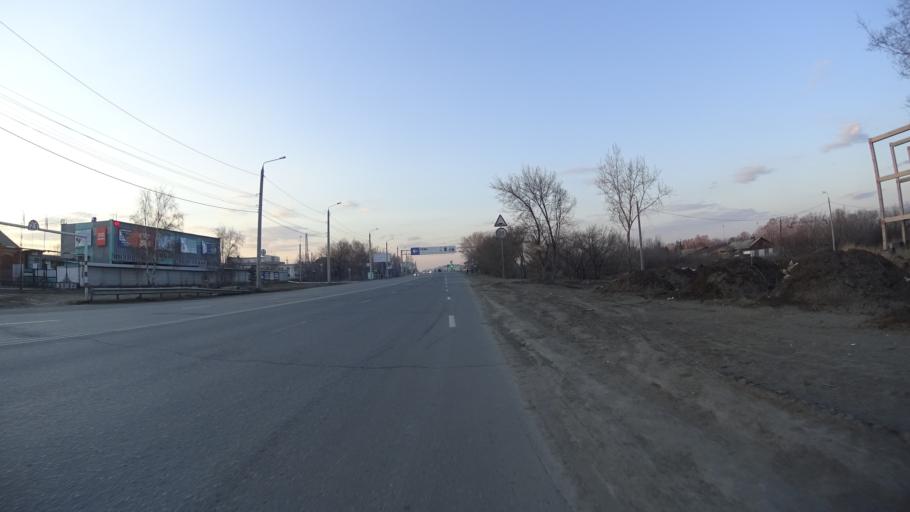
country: RU
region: Chelyabinsk
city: Novosineglazovskiy
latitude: 55.0849
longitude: 61.3883
